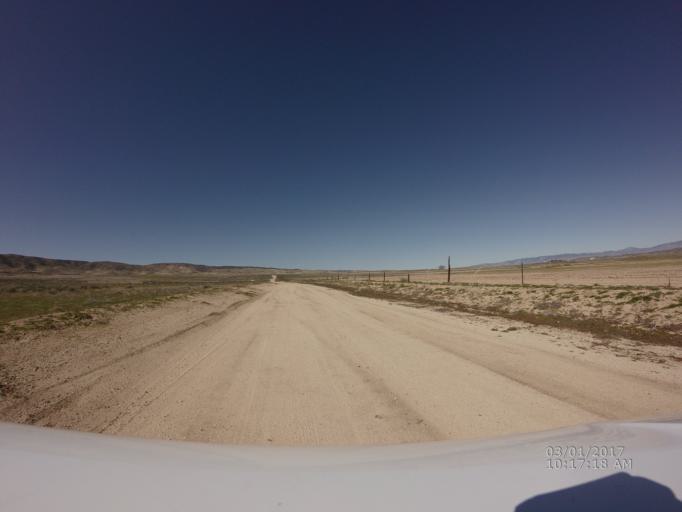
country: US
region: California
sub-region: Los Angeles County
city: Green Valley
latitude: 34.6891
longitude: -118.3584
